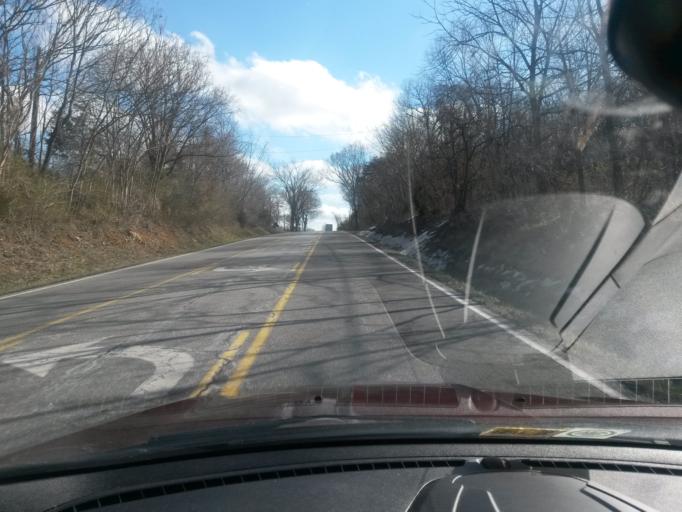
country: US
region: Virginia
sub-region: Augusta County
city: Jolivue
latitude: 38.1002
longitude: -79.0793
